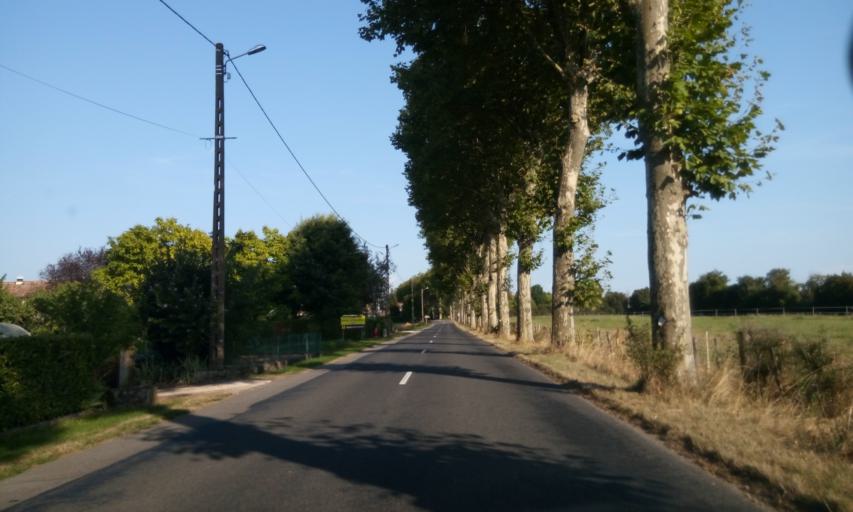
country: FR
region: Rhone-Alpes
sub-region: Departement de l'Ain
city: Amberieux-en-Dombes
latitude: 45.9994
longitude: 4.8940
